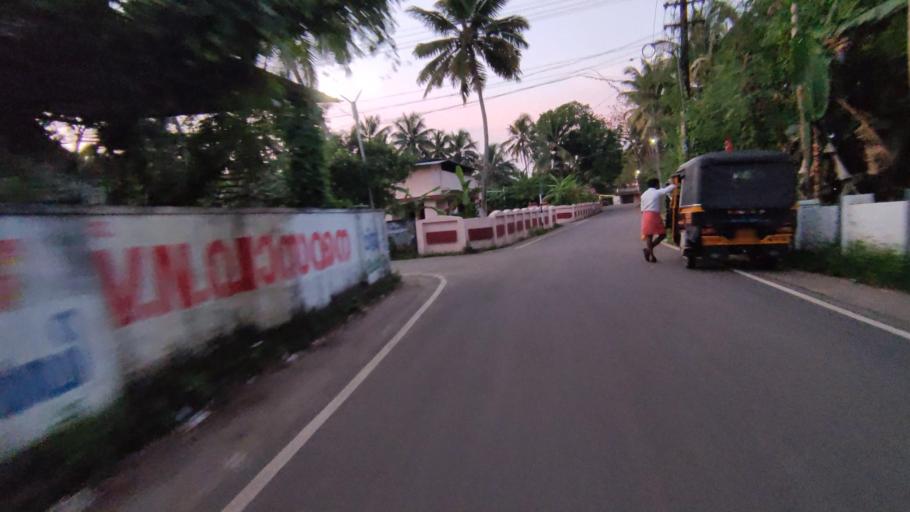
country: IN
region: Kerala
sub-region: Kottayam
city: Kottayam
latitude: 9.5814
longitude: 76.4354
